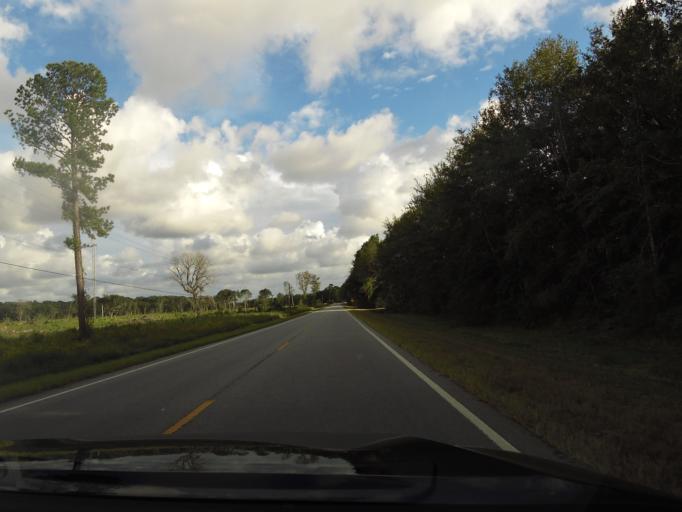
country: US
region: Georgia
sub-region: Liberty County
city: Midway
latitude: 31.7557
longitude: -81.4429
